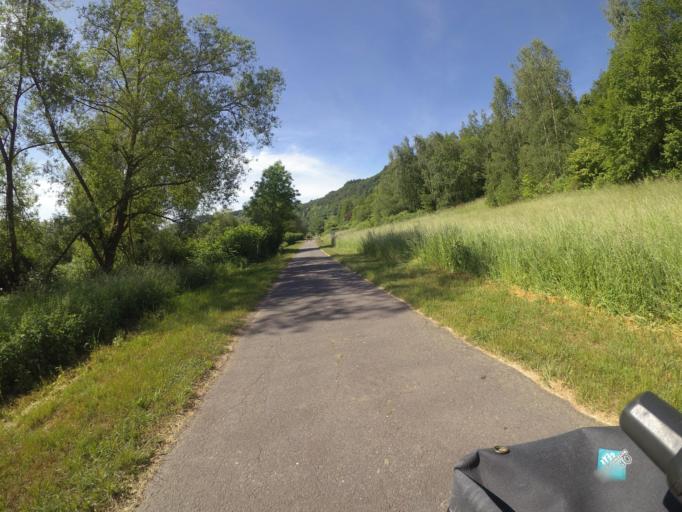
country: DE
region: Rheinland-Pfalz
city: Kanzem
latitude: 49.6726
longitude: 6.5584
